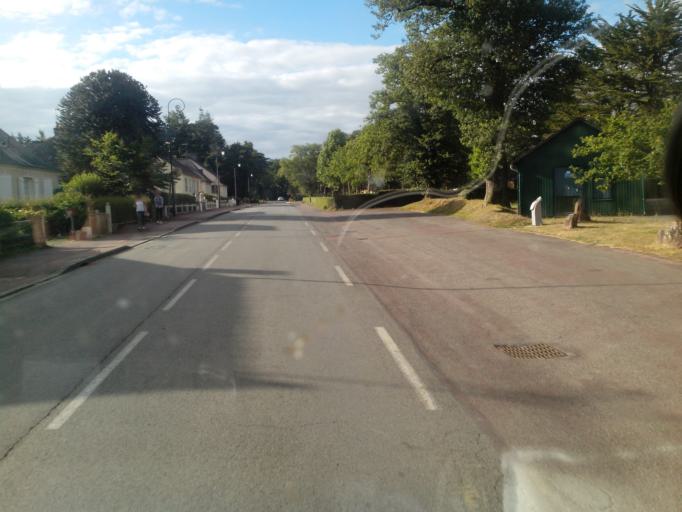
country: FR
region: Brittany
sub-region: Departement d'Ille-et-Vilaine
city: Paimpont
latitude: 48.0222
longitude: -2.1719
